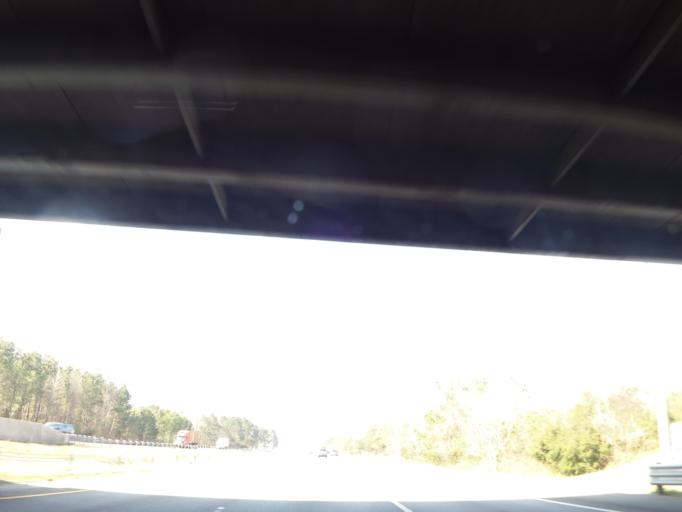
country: US
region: South Carolina
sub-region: Berkeley County
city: Ladson
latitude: 32.9987
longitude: -80.0939
